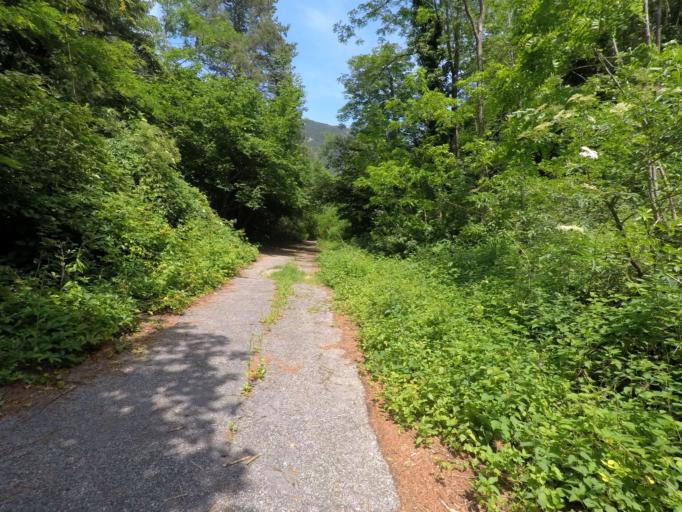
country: IT
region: Friuli Venezia Giulia
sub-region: Provincia di Udine
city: Amaro
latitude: 46.3840
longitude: 13.1388
